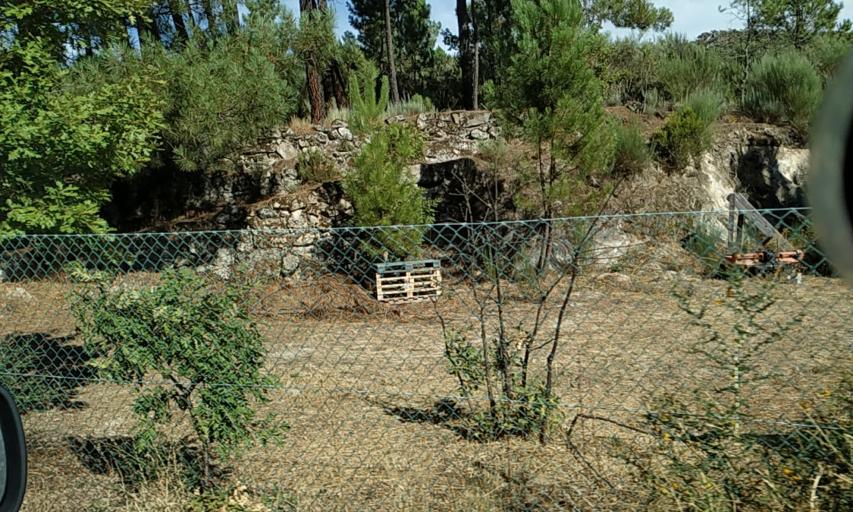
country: PT
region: Vila Real
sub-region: Sabrosa
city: Sabrosa
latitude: 41.3644
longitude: -7.5707
